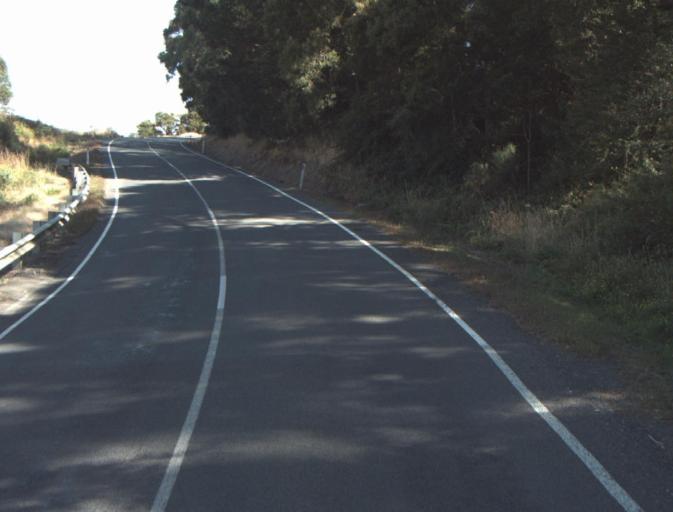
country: AU
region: Tasmania
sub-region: Launceston
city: Mayfield
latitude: -41.2276
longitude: 147.2088
